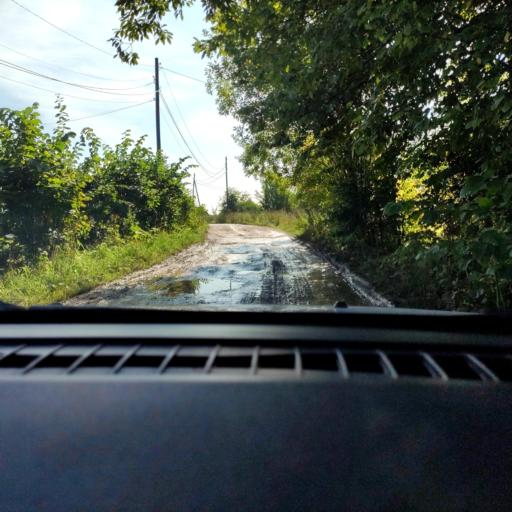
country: RU
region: Perm
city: Novyye Lyady
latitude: 58.0591
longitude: 56.5773
